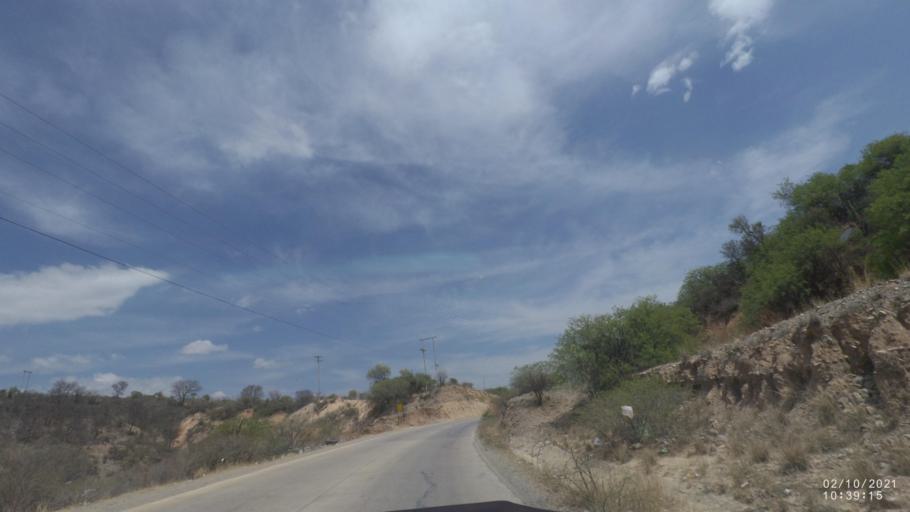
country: BO
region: Cochabamba
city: Capinota
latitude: -17.6301
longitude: -66.2724
